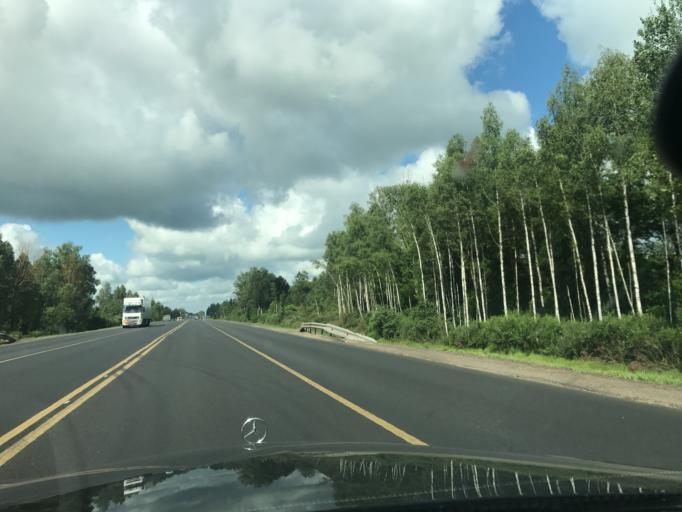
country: RU
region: Smolensk
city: Rudnya
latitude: 54.6976
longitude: 31.1403
